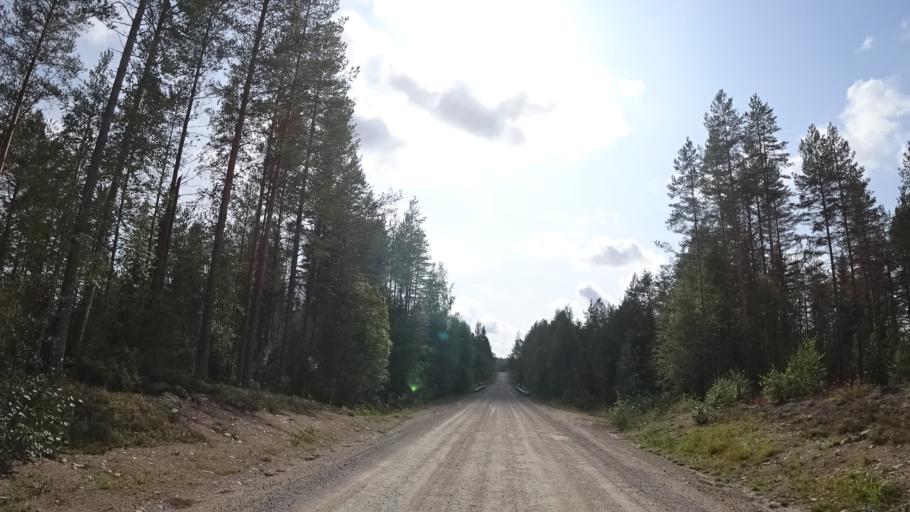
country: FI
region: North Karelia
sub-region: Pielisen Karjala
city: Lieksa
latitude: 63.5761
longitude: 30.1229
